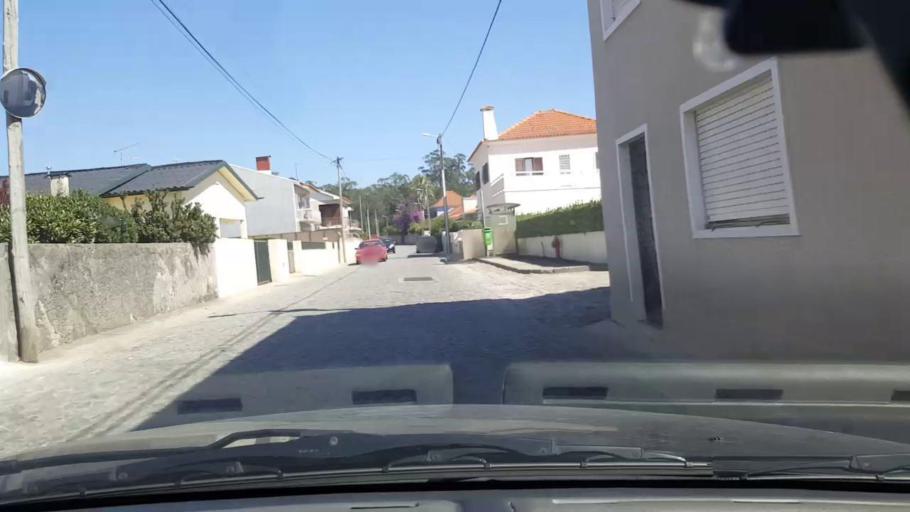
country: PT
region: Porto
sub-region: Matosinhos
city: Lavra
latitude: 41.2976
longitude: -8.7174
